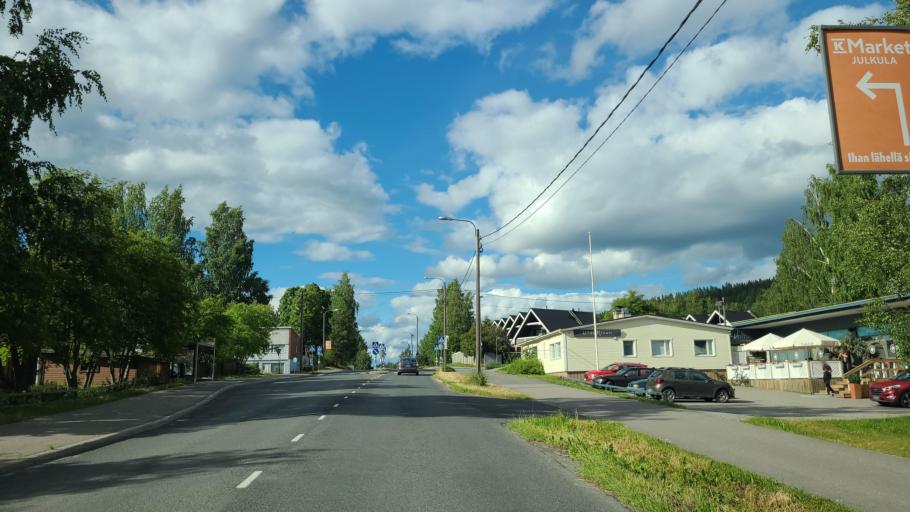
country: FI
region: Northern Savo
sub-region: Kuopio
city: Kuopio
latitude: 62.9248
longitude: 27.6322
